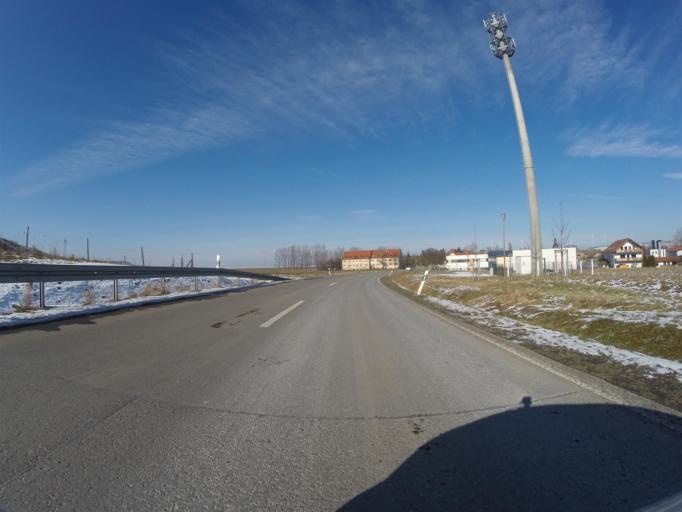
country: DE
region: Thuringia
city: Bucha
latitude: 50.8763
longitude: 11.5116
